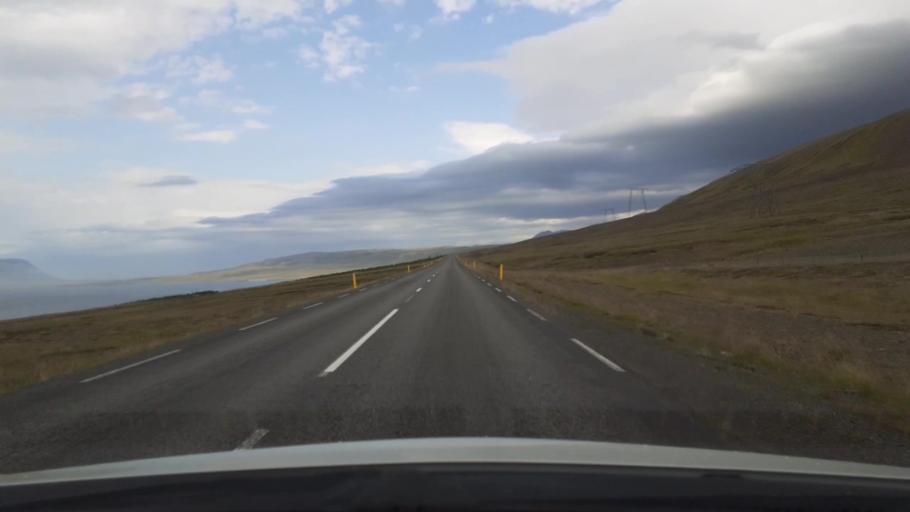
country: IS
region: Capital Region
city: Mosfellsbaer
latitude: 64.4015
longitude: -21.5480
